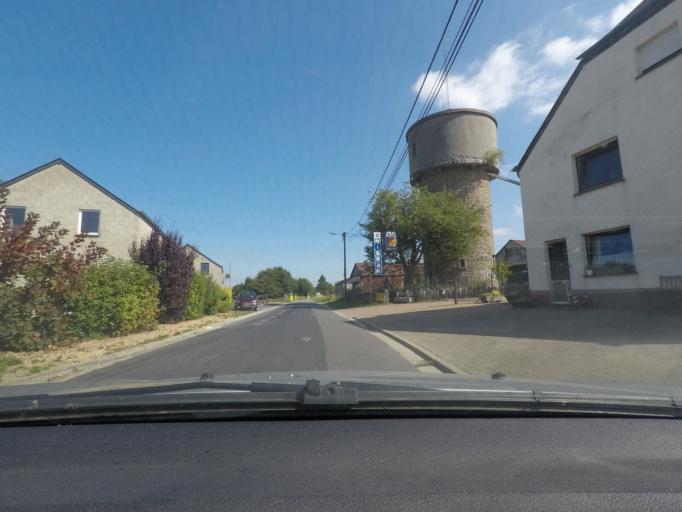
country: BE
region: Wallonia
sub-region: Province du Luxembourg
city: Fauvillers
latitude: 49.7932
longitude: 5.6283
